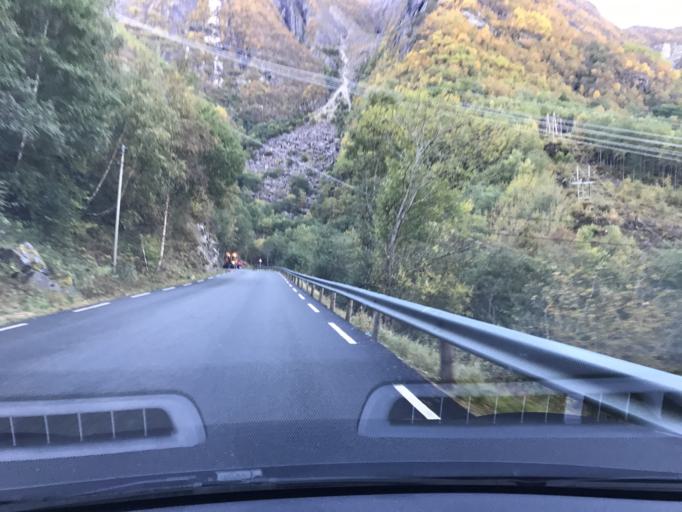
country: NO
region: Sogn og Fjordane
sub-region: Aurland
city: Aurlandsvangen
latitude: 60.8620
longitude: 7.3046
